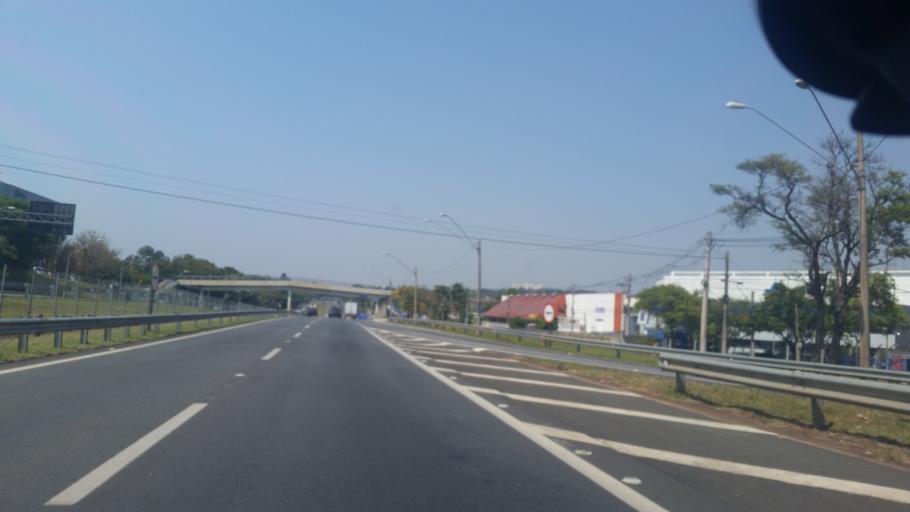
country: BR
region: Sao Paulo
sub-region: Campinas
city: Campinas
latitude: -22.8480
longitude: -47.0781
